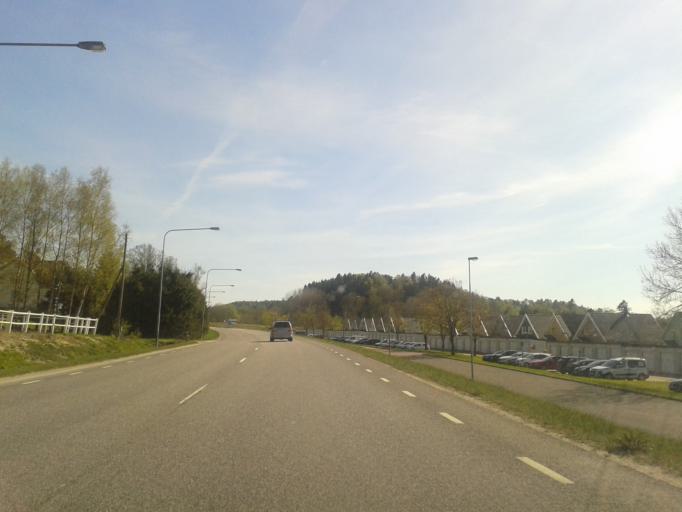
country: SE
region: Vaestra Goetaland
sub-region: Ale Kommun
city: Nodinge-Nol
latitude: 57.8937
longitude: 12.0679
